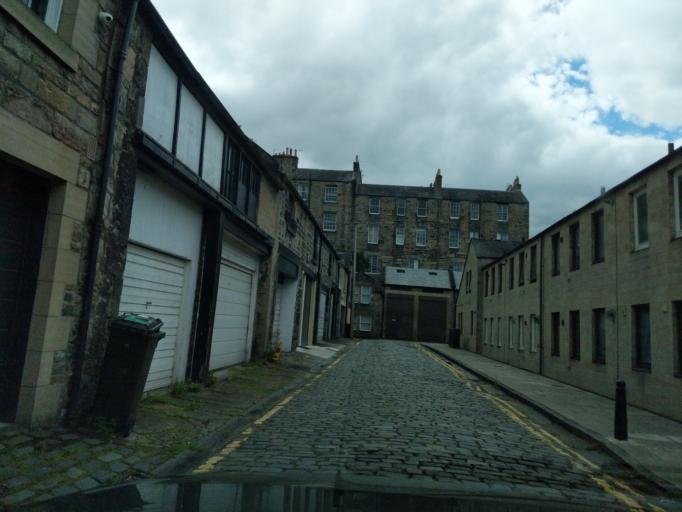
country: GB
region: Scotland
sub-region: Edinburgh
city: Edinburgh
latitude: 55.9556
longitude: -3.2041
